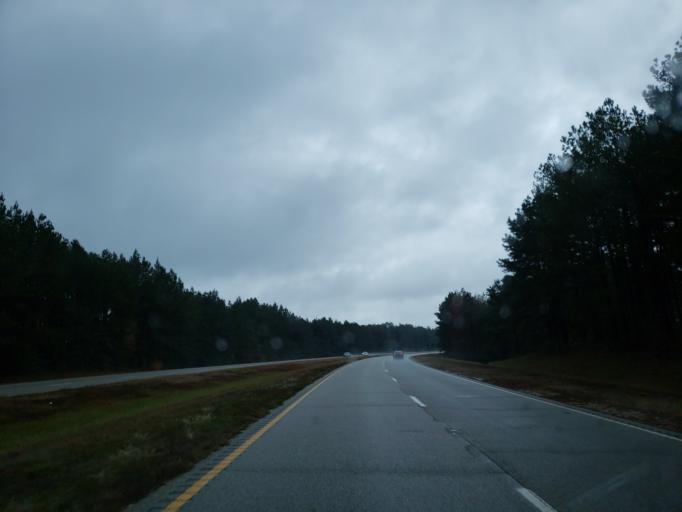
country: US
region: Mississippi
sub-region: Lauderdale County
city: Meridian
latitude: 32.2822
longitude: -88.6977
